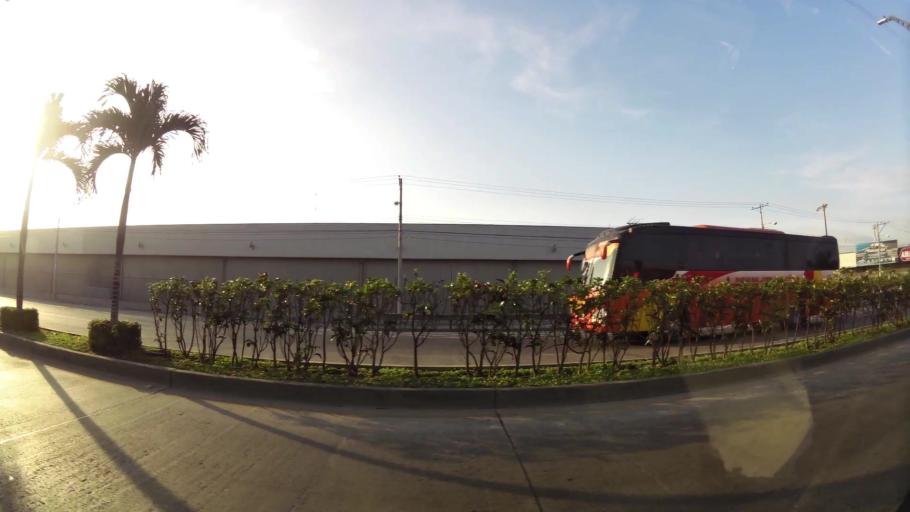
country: EC
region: Guayas
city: Eloy Alfaro
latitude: -2.1528
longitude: -79.8781
